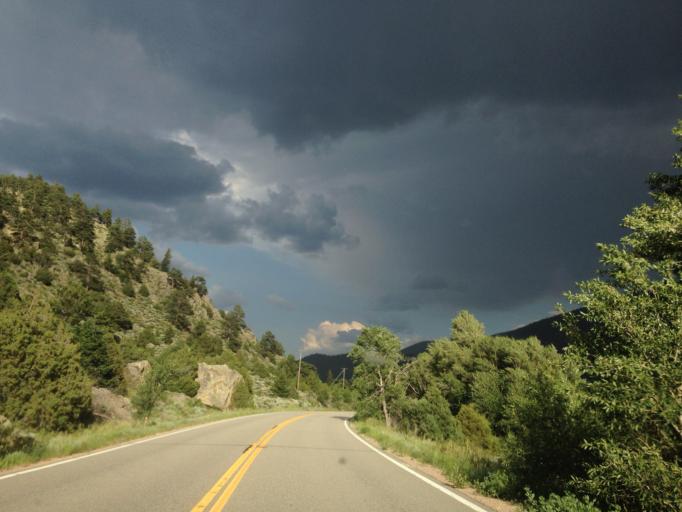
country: US
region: Colorado
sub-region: Larimer County
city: Estes Park
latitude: 40.6995
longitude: -105.7013
